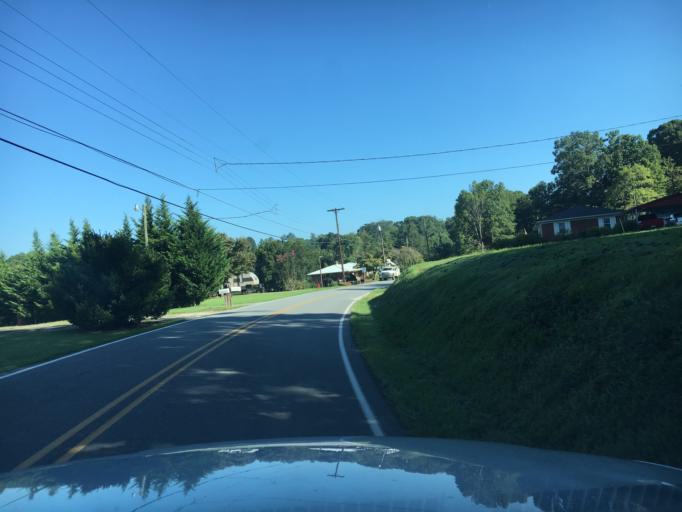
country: US
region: North Carolina
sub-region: McDowell County
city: West Marion
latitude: 35.6528
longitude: -82.0239
